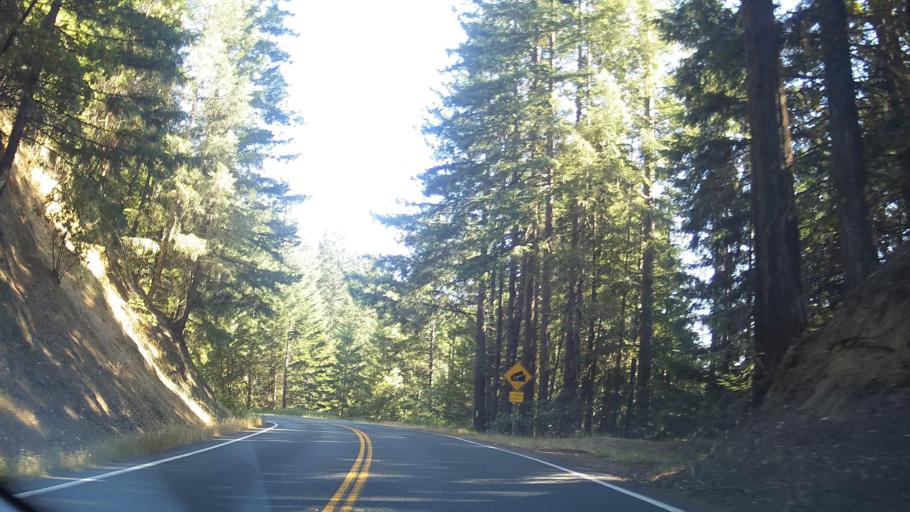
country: US
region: California
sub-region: Mendocino County
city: Brooktrails
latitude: 39.3930
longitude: -123.4662
